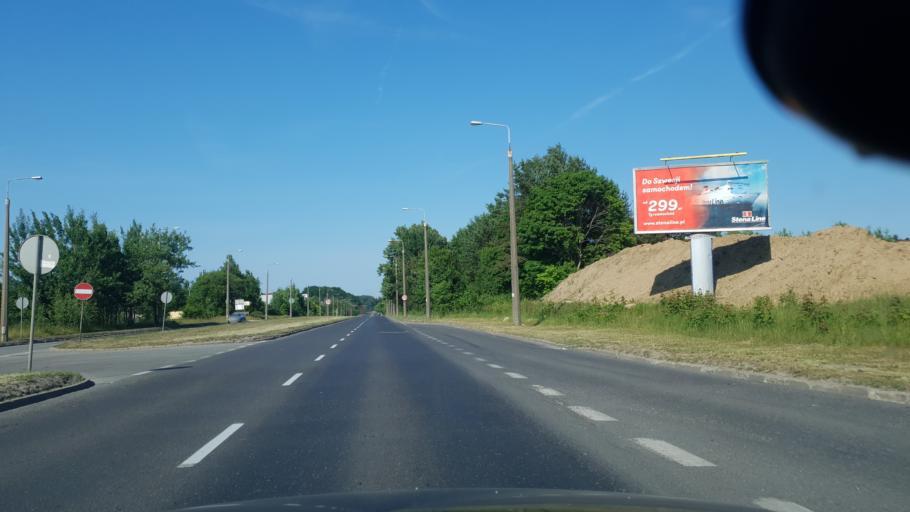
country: PL
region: Pomeranian Voivodeship
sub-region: Gdynia
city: Wielki Kack
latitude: 54.4606
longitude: 18.4570
